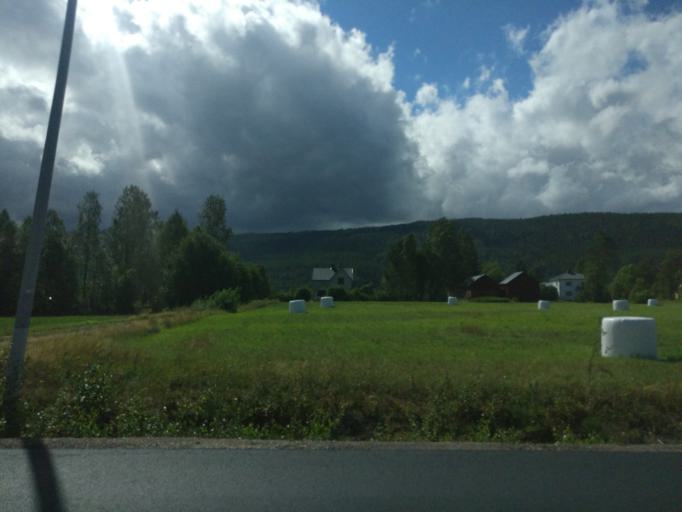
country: SE
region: Vaermland
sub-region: Hagfors Kommun
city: Ekshaerad
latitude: 60.3537
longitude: 13.3315
